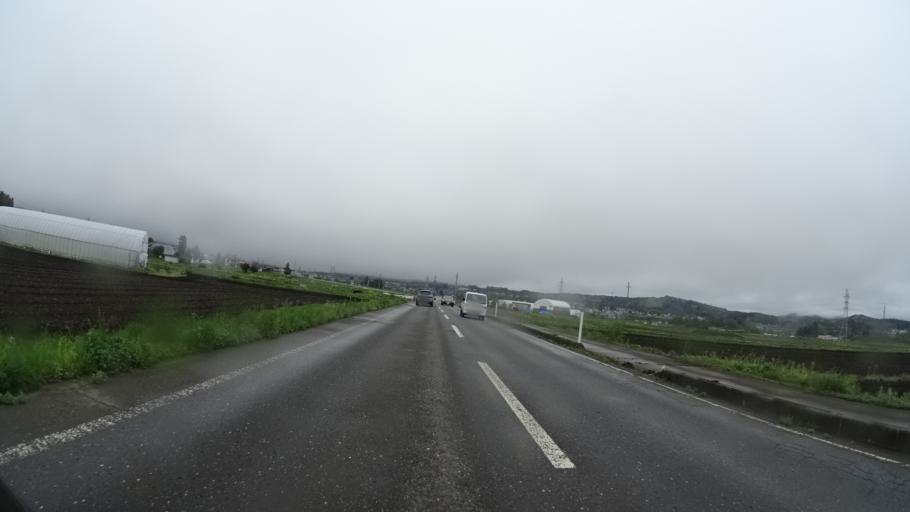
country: JP
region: Nagano
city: Nagano-shi
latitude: 36.7952
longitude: 138.1958
